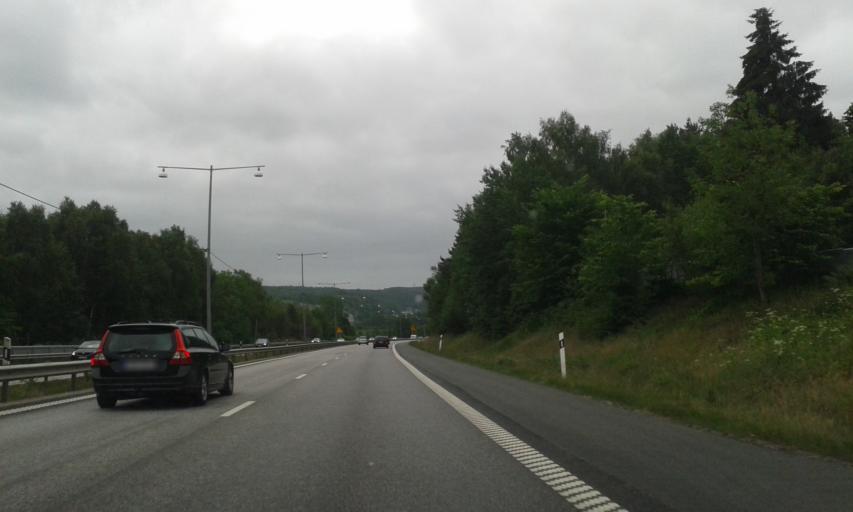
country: SE
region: Vaestra Goetaland
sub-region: Kungalvs Kommun
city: Kungalv
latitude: 57.8537
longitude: 11.9963
